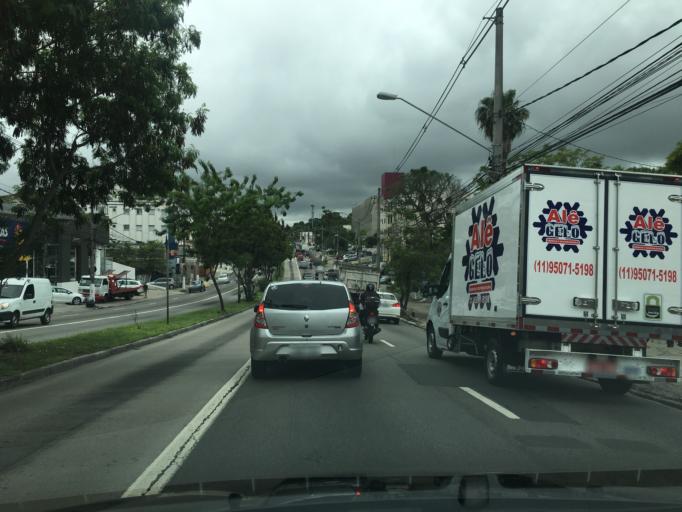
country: BR
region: Sao Paulo
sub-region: Taboao Da Serra
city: Taboao da Serra
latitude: -23.5837
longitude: -46.7160
